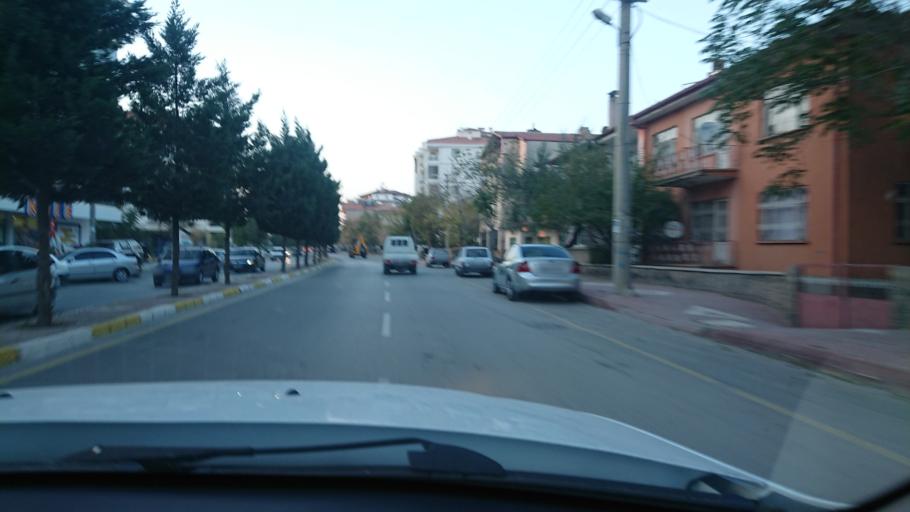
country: TR
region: Aksaray
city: Aksaray
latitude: 38.3619
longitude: 34.0368
